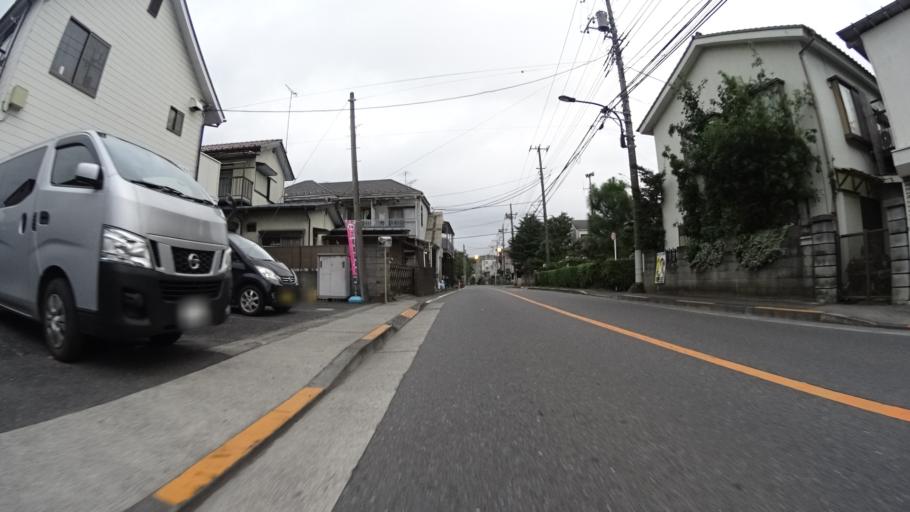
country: JP
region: Tokyo
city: Fussa
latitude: 35.7507
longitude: 139.3155
